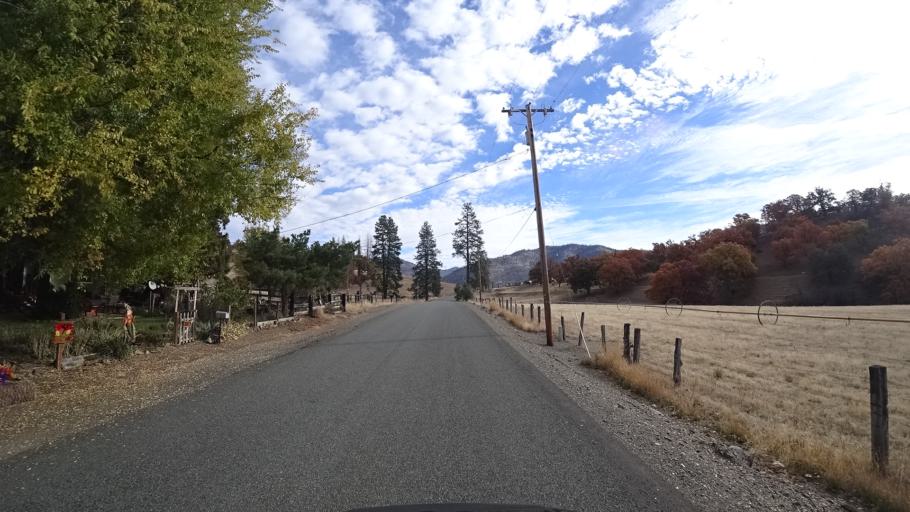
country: US
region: California
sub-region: Siskiyou County
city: Yreka
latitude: 41.6250
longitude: -122.7836
